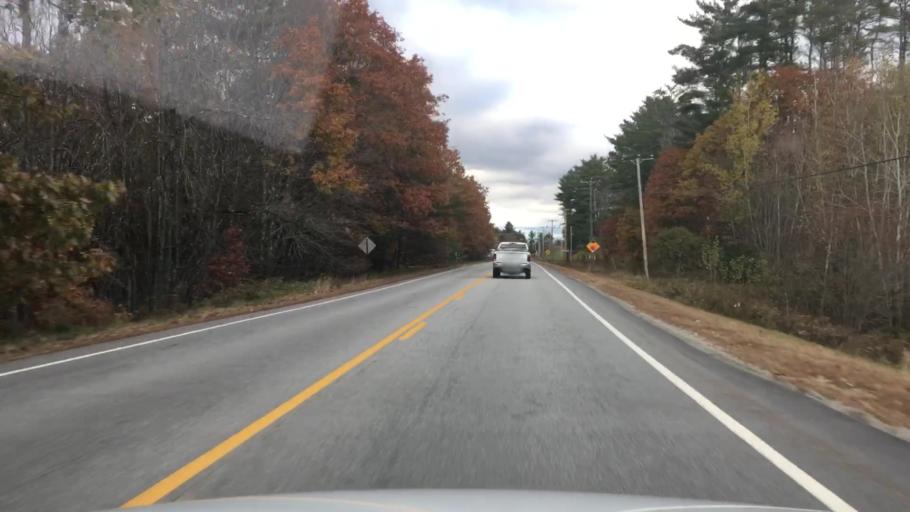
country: US
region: Maine
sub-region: Androscoggin County
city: Leeds
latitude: 44.3394
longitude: -70.1321
